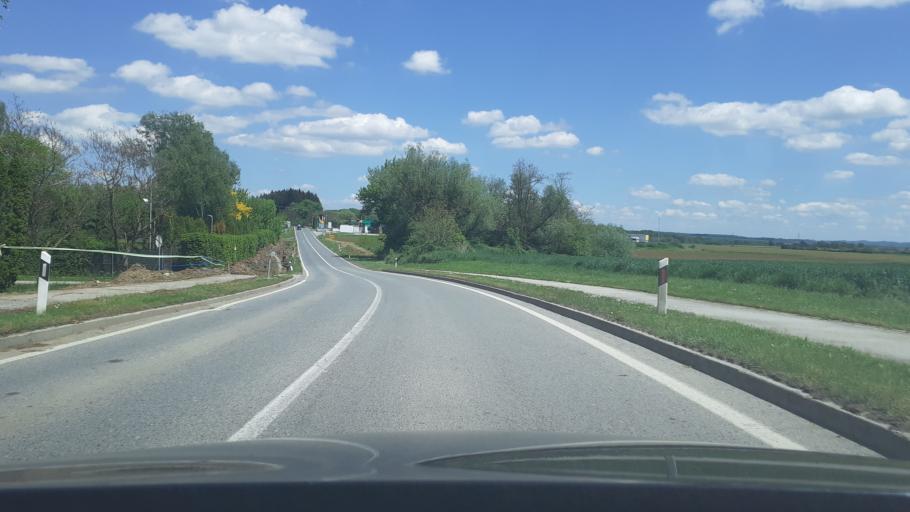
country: HR
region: Pozesko-Slavonska
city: Vidovci
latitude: 45.3425
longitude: 17.7108
